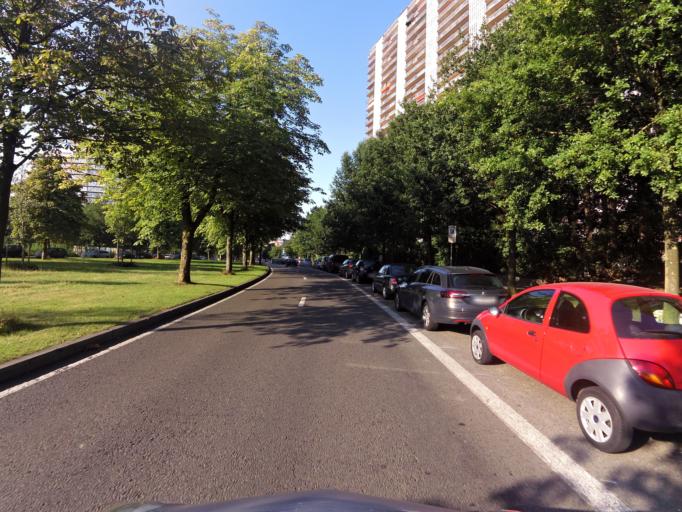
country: BE
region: Flanders
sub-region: Provincie Vlaams-Brabant
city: Dilbeek
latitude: 50.8538
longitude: 4.3024
